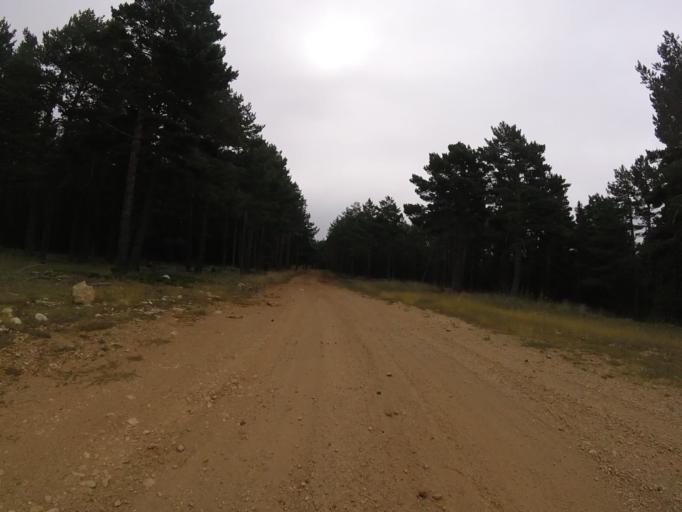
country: ES
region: Aragon
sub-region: Provincia de Teruel
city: Valdelinares
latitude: 40.3711
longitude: -0.6223
